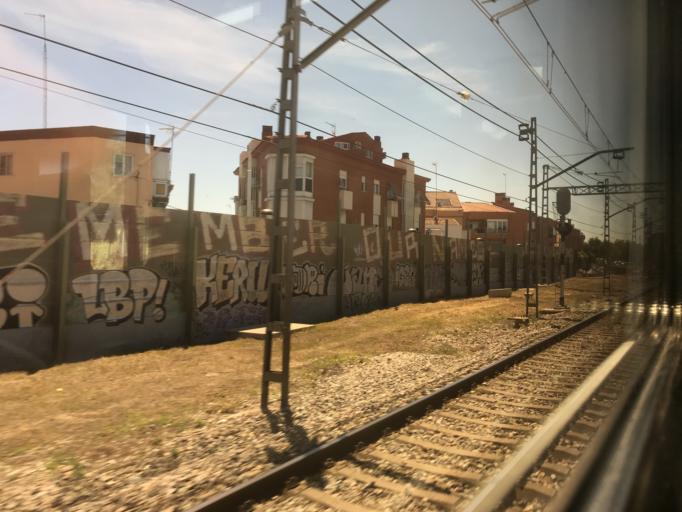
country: ES
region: Madrid
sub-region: Provincia de Madrid
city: Pinto
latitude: 40.2468
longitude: -3.7039
